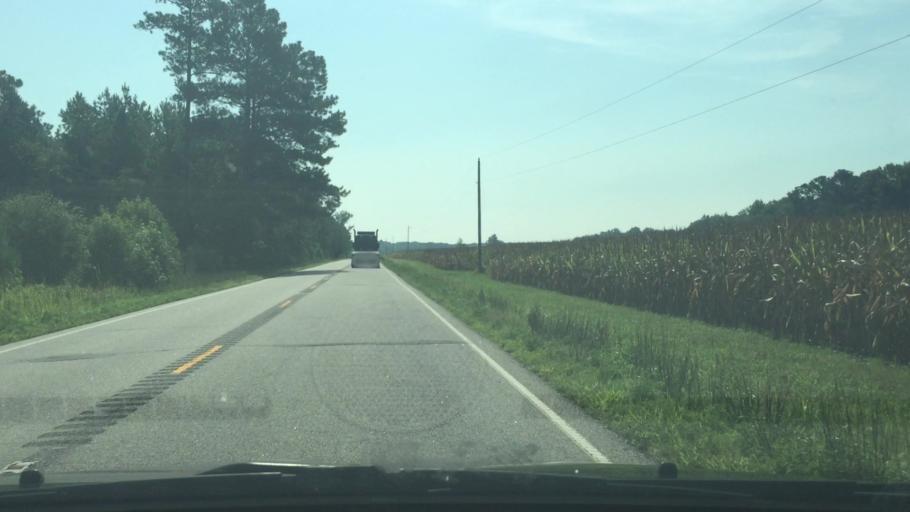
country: US
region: Virginia
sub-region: Sussex County
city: Sussex
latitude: 36.9815
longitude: -77.2376
